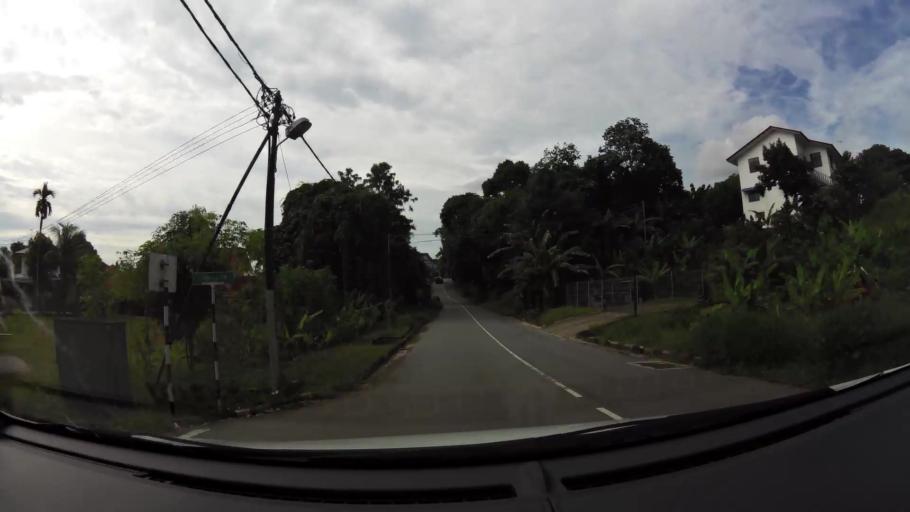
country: BN
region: Brunei and Muara
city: Bandar Seri Begawan
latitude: 4.8979
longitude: 114.8958
